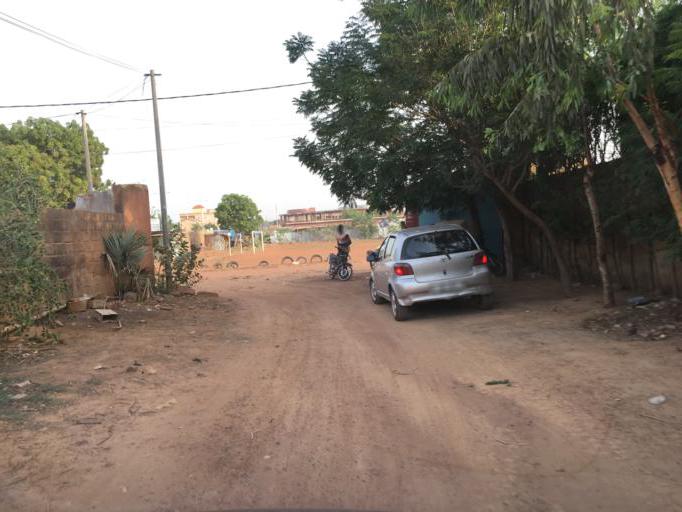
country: BF
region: Centre
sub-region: Kadiogo Province
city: Ouagadougou
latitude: 12.3647
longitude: -1.4982
